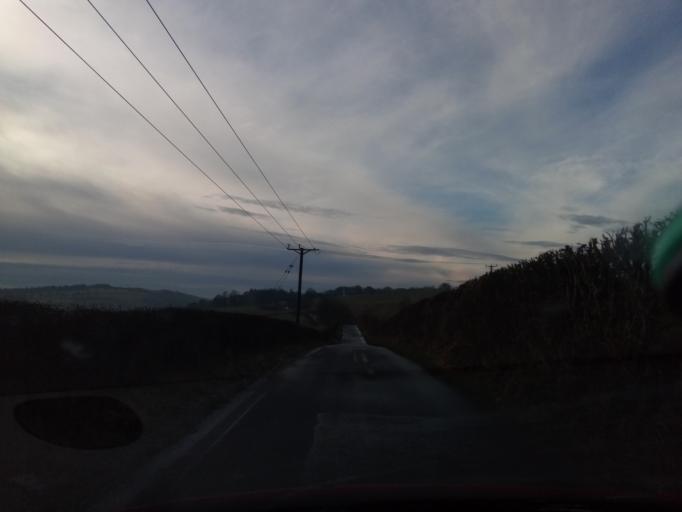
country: GB
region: Scotland
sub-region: The Scottish Borders
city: Hawick
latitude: 55.4480
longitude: -2.7418
